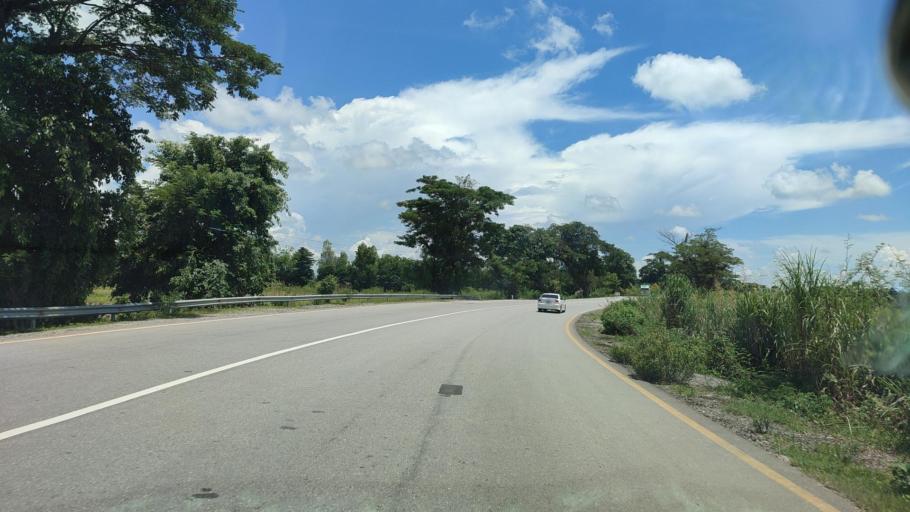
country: MM
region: Bago
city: Nyaunglebin
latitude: 18.1789
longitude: 96.5969
